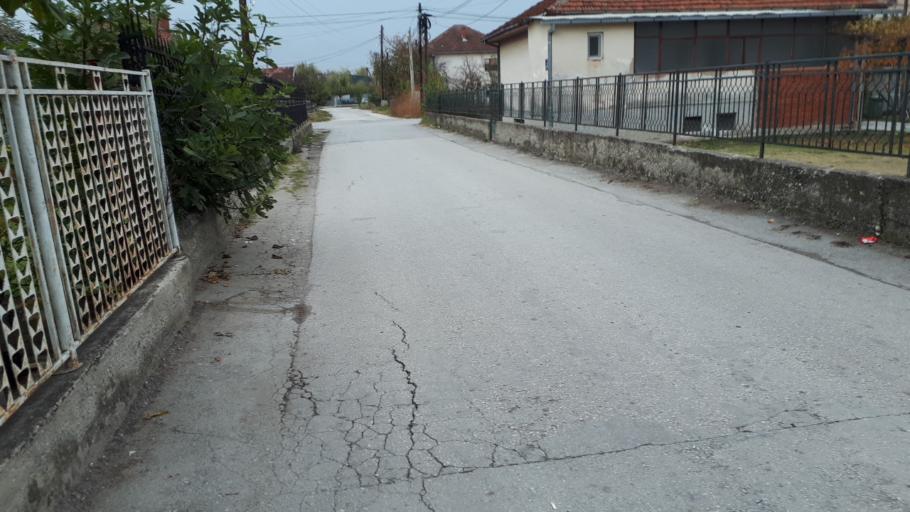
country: MK
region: Saraj
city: Saraj
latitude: 42.0203
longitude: 21.3571
